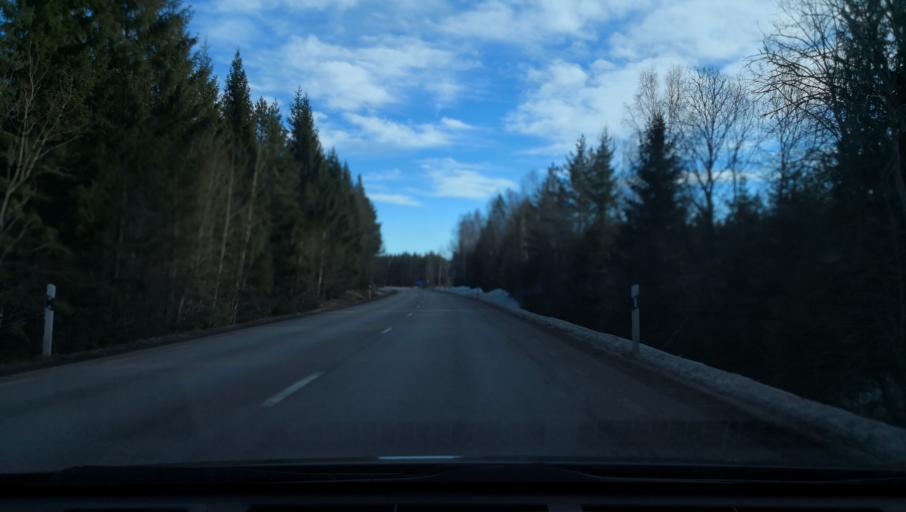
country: SE
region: Uppsala
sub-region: Osthammars Kommun
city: Osterbybruk
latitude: 60.1762
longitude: 17.9186
